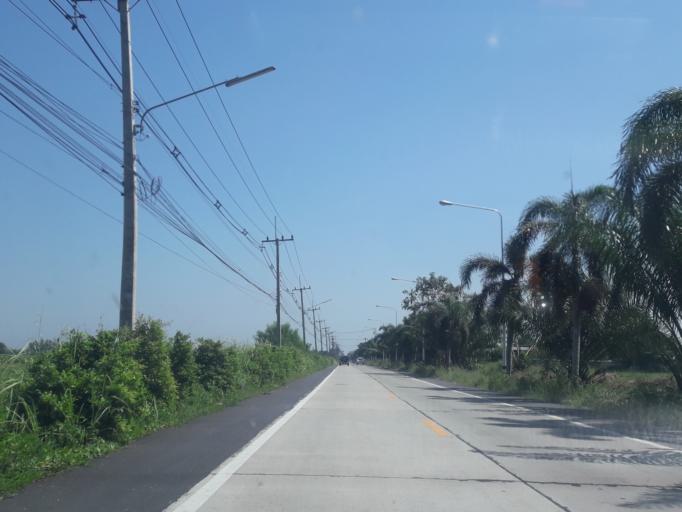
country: TH
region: Pathum Thani
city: Nong Suea
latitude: 14.1363
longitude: 100.8604
